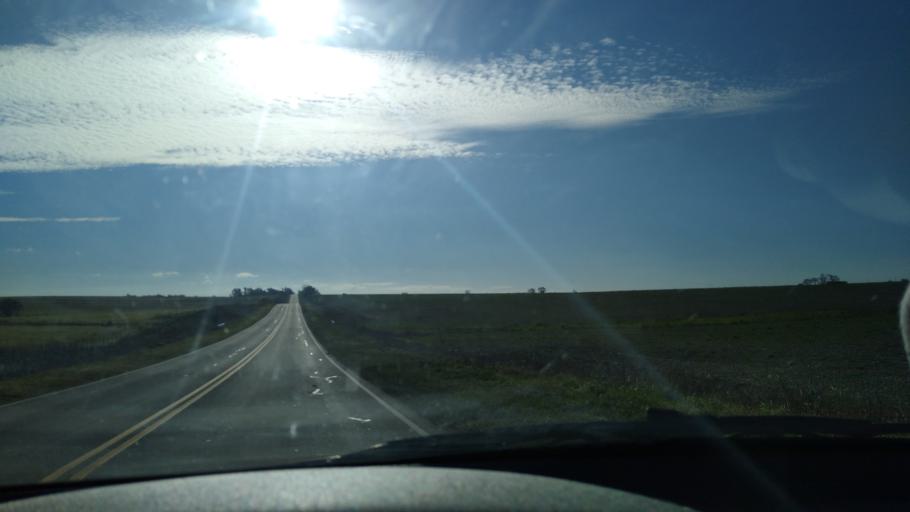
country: AR
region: Entre Rios
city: Aranguren
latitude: -32.3429
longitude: -60.3725
